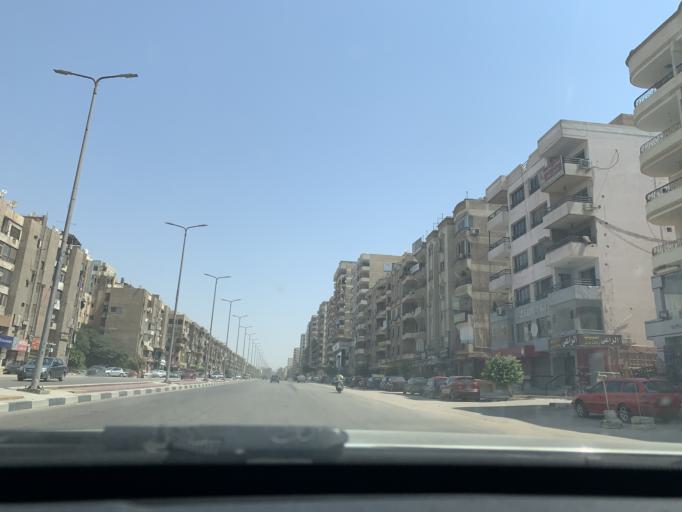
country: EG
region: Muhafazat al Qahirah
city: Cairo
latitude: 30.0564
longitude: 31.3629
